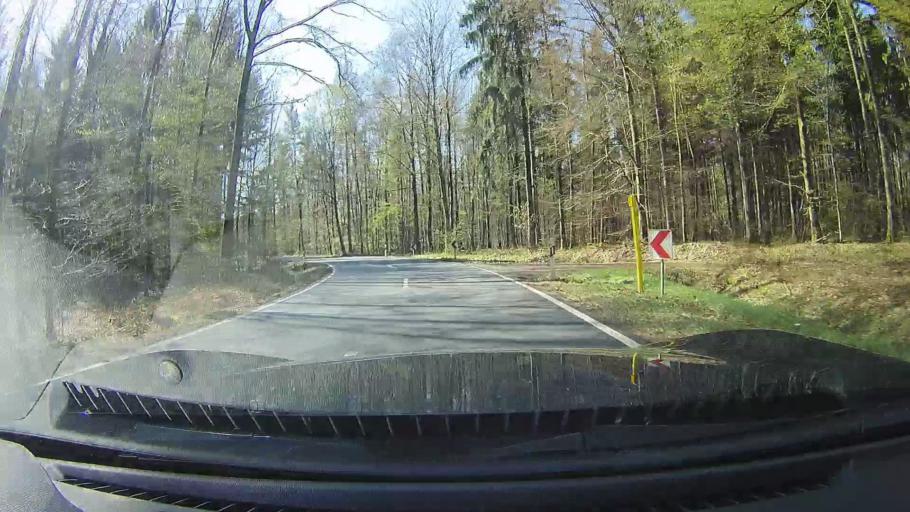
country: DE
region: Baden-Wuerttemberg
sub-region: Karlsruhe Region
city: Neunkirchen
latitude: 49.4172
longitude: 8.9834
